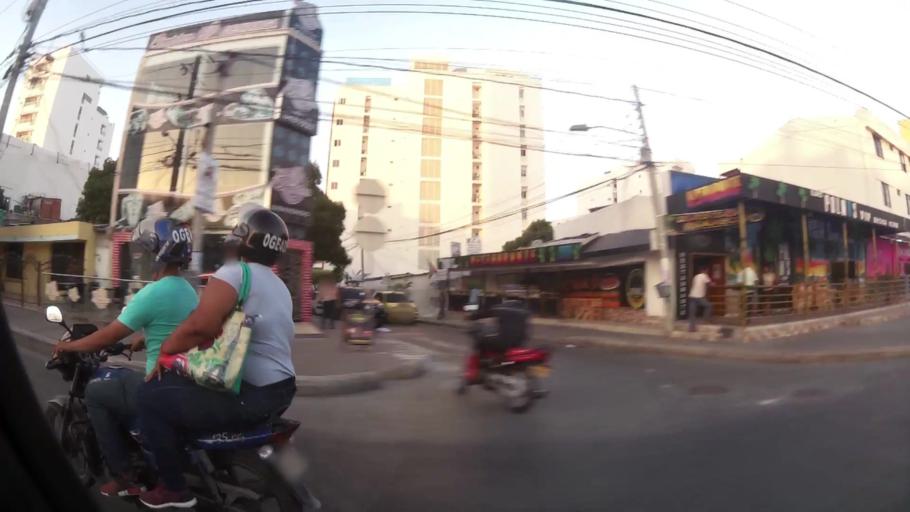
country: CO
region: Bolivar
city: Cartagena
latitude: 10.3950
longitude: -75.4900
